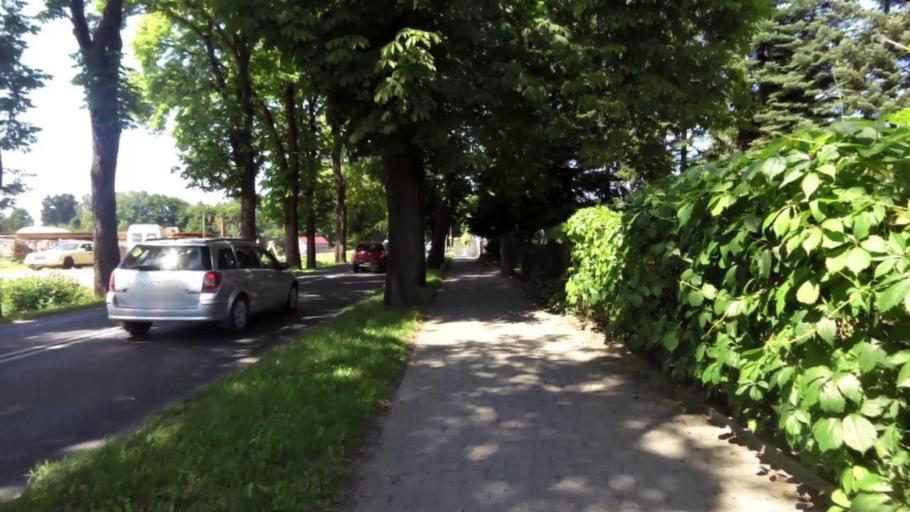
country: PL
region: West Pomeranian Voivodeship
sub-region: Powiat swidwinski
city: Polczyn-Zdroj
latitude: 53.7704
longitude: 16.0905
